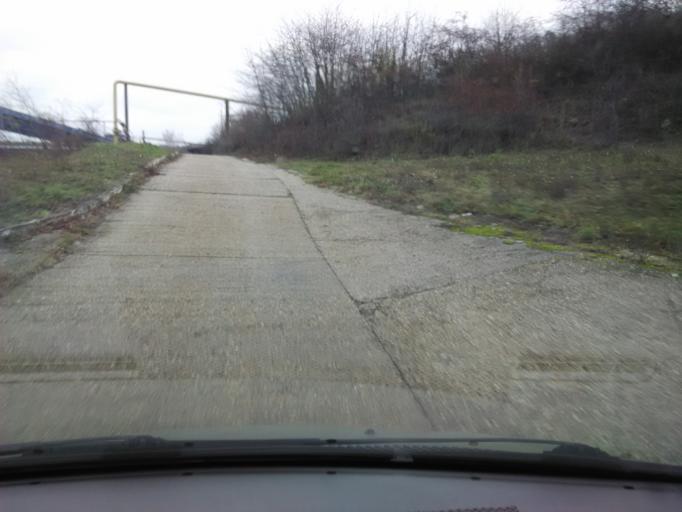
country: SK
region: Nitriansky
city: Tlmace
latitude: 48.2935
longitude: 18.5446
